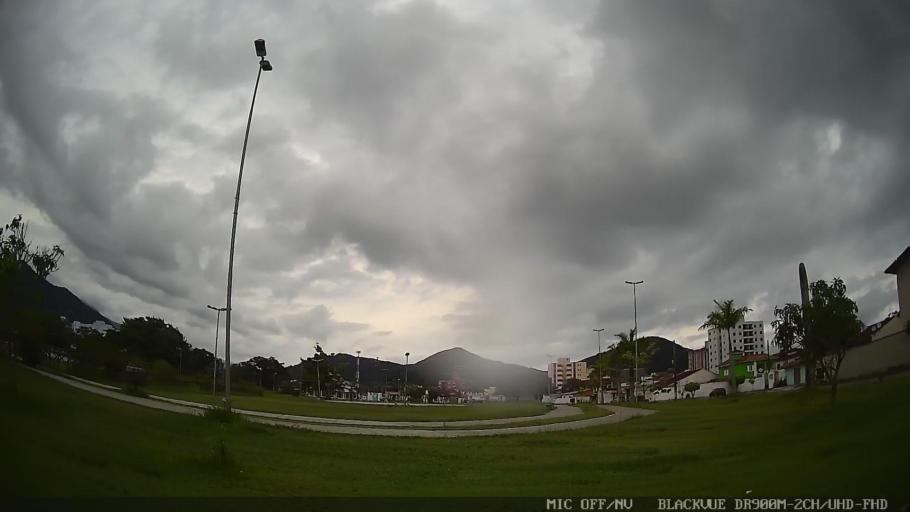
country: BR
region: Sao Paulo
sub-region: Caraguatatuba
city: Caraguatatuba
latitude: -23.6249
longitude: -45.3894
